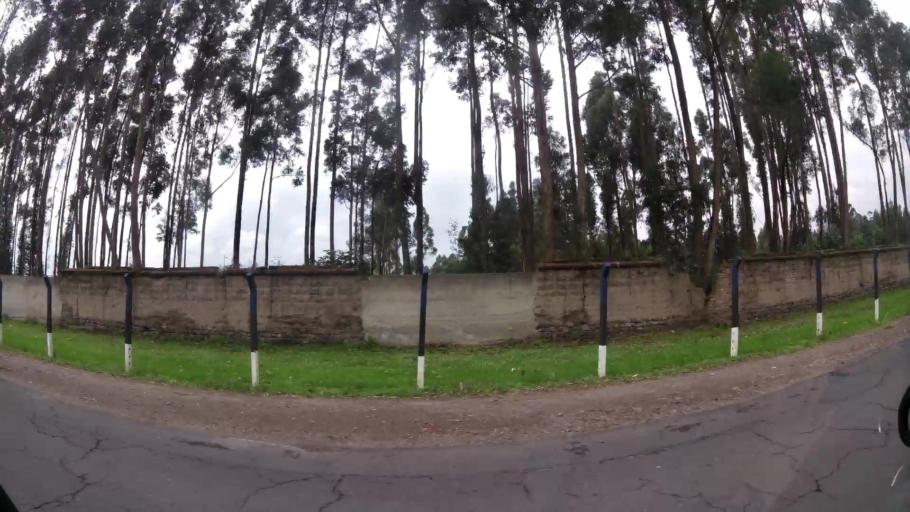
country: EC
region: Pichincha
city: Sangolqui
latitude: -0.3482
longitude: -78.4716
